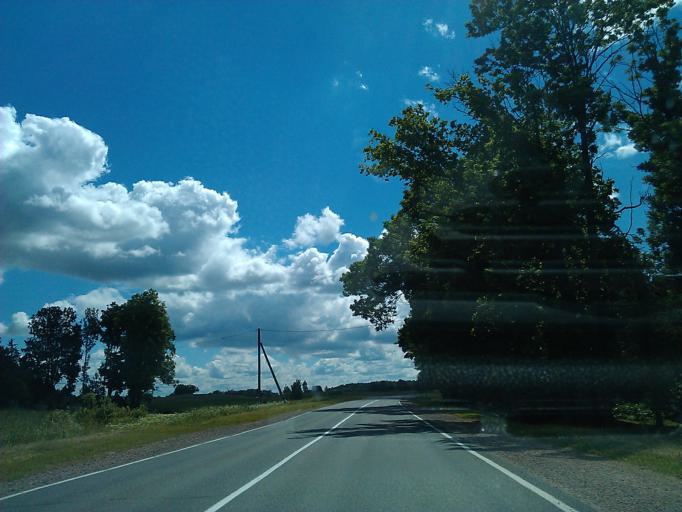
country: LV
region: Vilanu
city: Vilani
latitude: 56.5963
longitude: 26.8752
